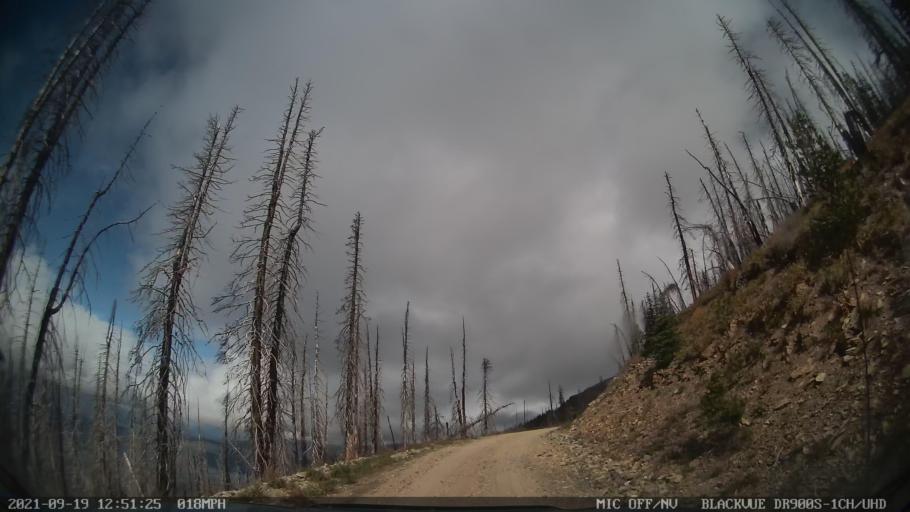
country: US
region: Montana
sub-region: Missoula County
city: Seeley Lake
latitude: 47.1894
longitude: -113.3603
